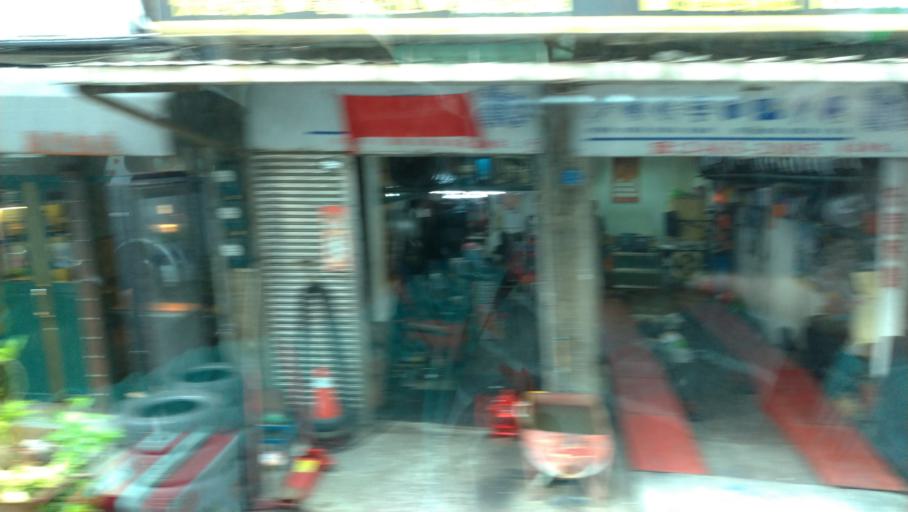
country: TW
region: Taiwan
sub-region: Keelung
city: Keelung
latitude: 25.1524
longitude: 121.7690
